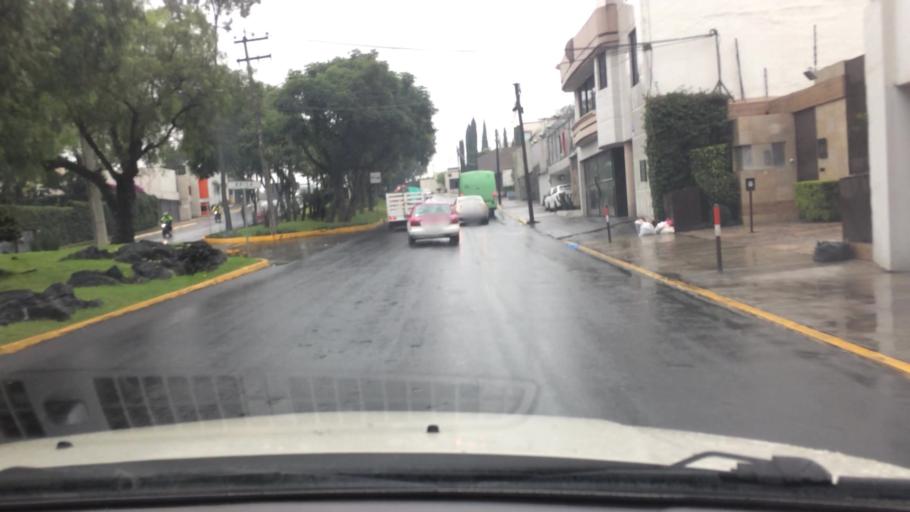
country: MX
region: Mexico City
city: Magdalena Contreras
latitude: 19.3320
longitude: -99.2002
